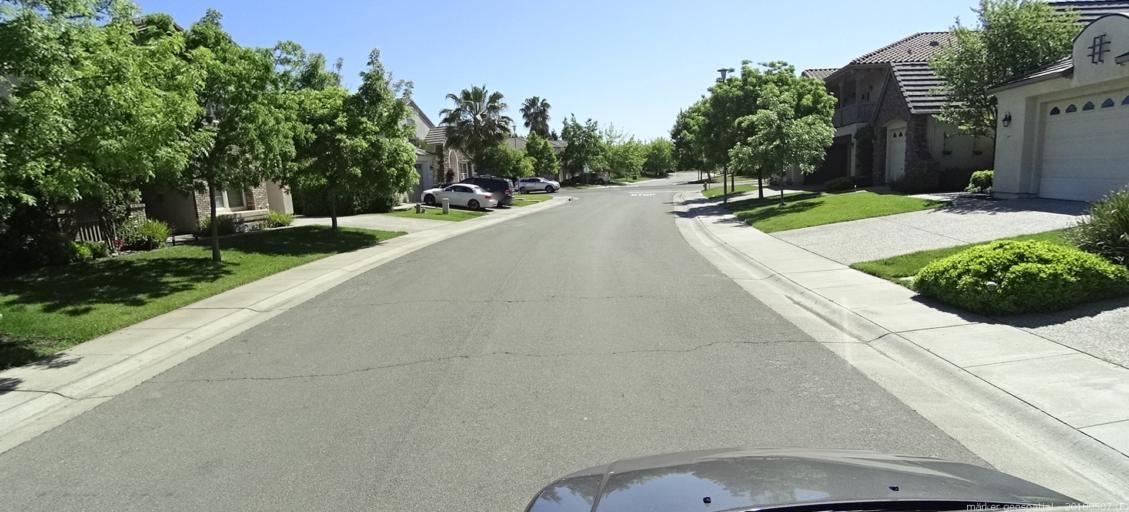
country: US
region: California
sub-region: Sacramento County
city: Rio Linda
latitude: 38.6618
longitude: -121.4963
